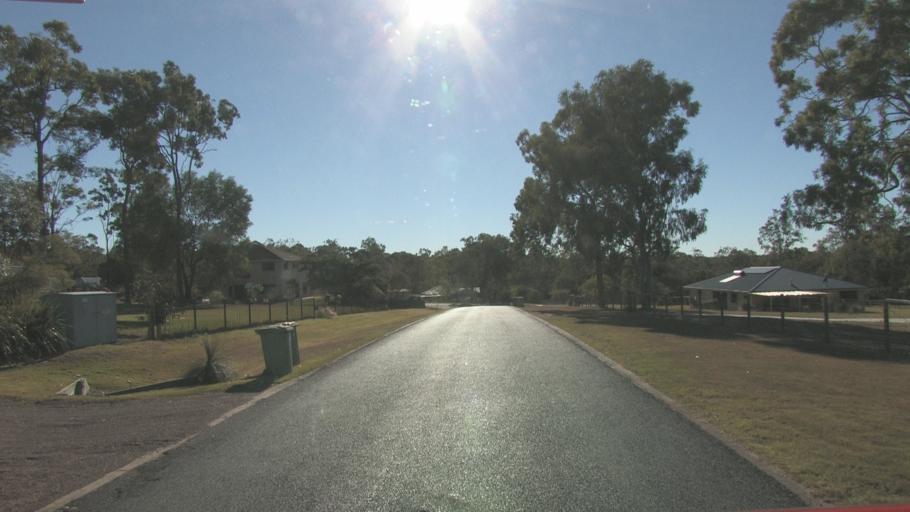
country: AU
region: Queensland
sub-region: Logan
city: North Maclean
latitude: -27.7433
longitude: 152.9632
